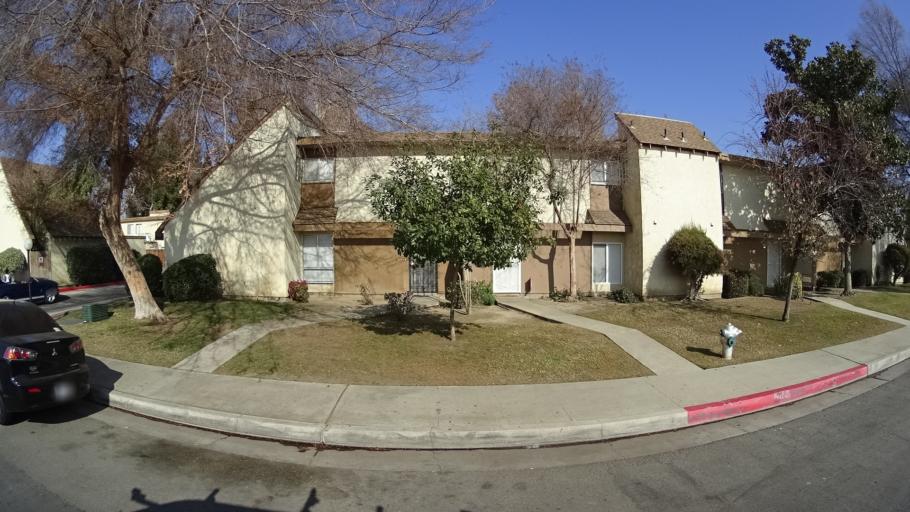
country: US
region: California
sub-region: Kern County
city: Bakersfield
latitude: 35.3455
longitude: -119.0563
